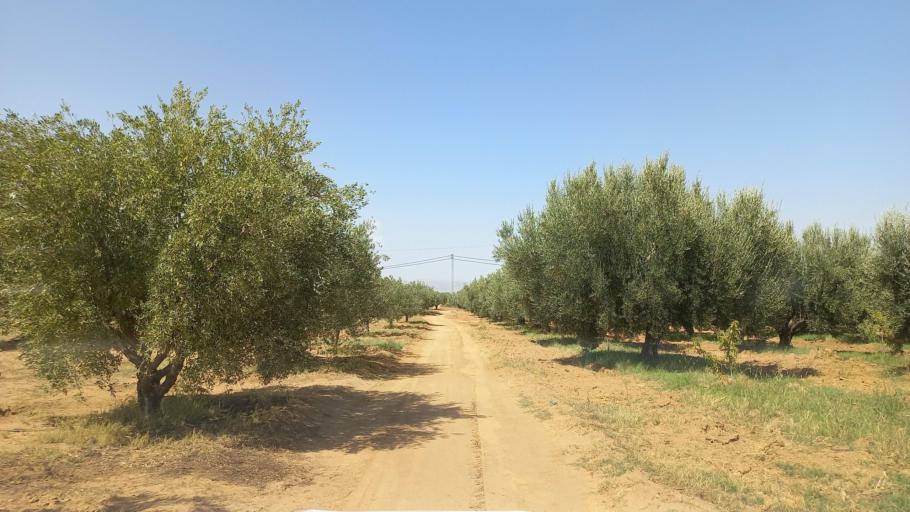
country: TN
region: Al Qasrayn
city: Kasserine
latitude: 35.2214
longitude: 9.0429
